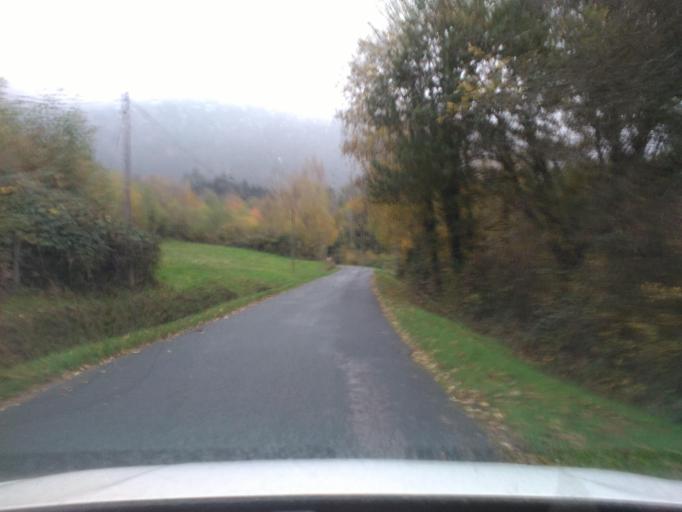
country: FR
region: Lorraine
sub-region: Departement des Vosges
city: Sainte-Marguerite
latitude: 48.2939
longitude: 7.0065
